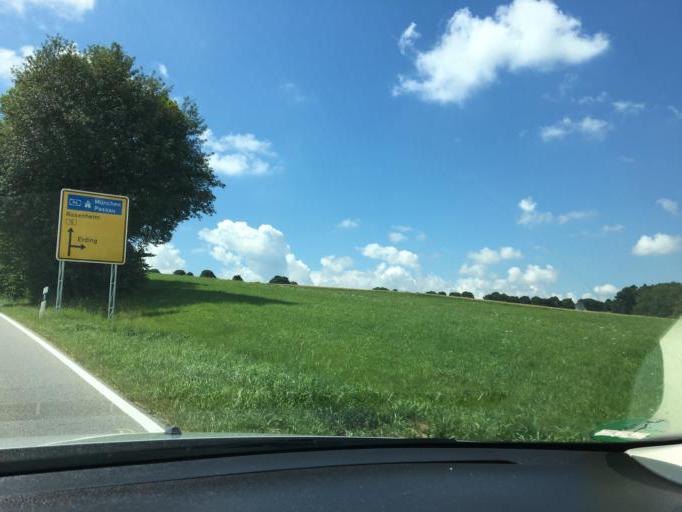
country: DE
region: Bavaria
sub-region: Upper Bavaria
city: Dorfen
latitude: 48.2905
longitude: 12.1261
